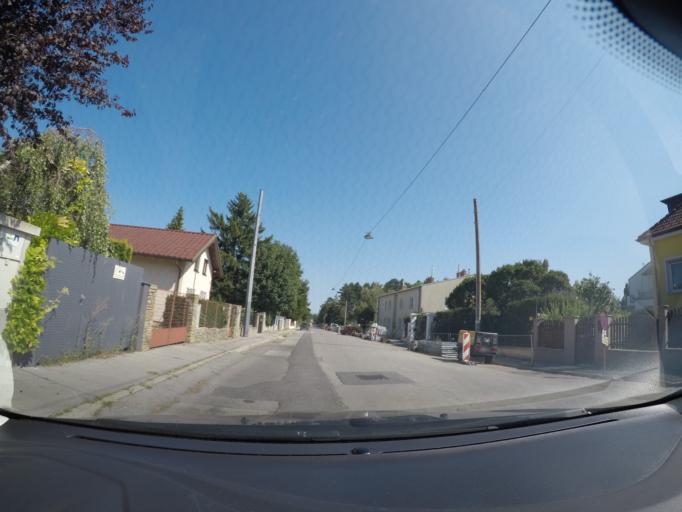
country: AT
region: Lower Austria
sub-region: Politischer Bezirk Modling
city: Perchtoldsdorf
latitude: 48.1586
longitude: 16.2667
